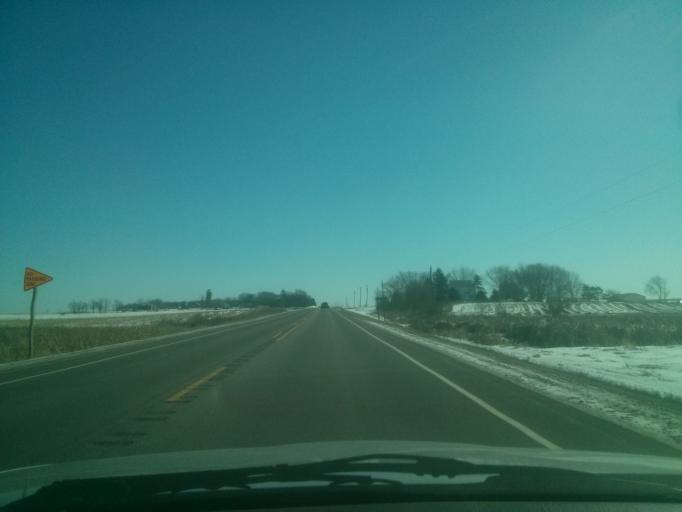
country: US
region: Wisconsin
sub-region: Polk County
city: Clear Lake
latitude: 45.1364
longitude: -92.3260
